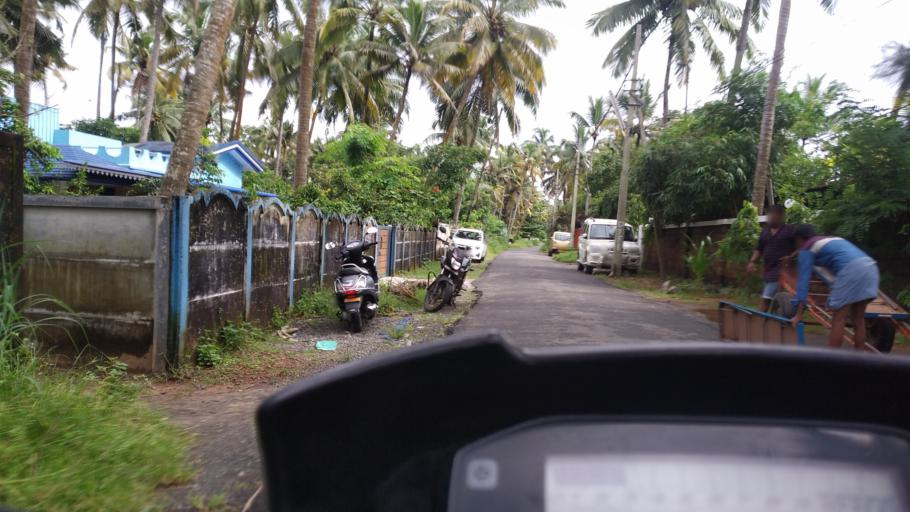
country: IN
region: Kerala
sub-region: Thrissur District
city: Kodungallur
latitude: 10.1619
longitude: 76.1713
